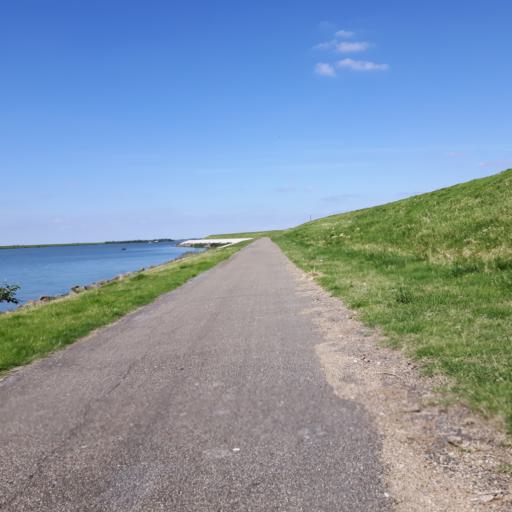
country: NL
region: Zeeland
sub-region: Gemeente Tholen
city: Tholen
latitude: 51.4704
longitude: 4.2304
